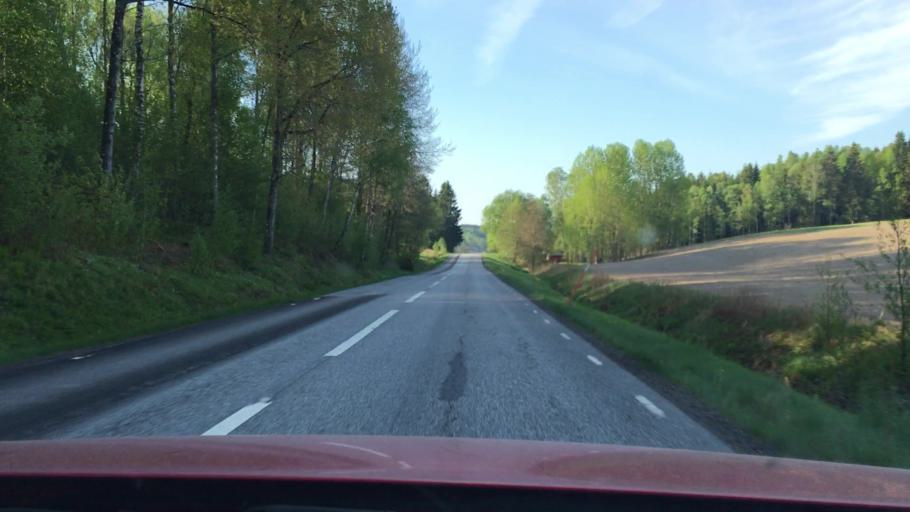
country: SE
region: Vaestra Goetaland
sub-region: Munkedals Kommun
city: Munkedal
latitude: 58.6164
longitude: 11.5586
